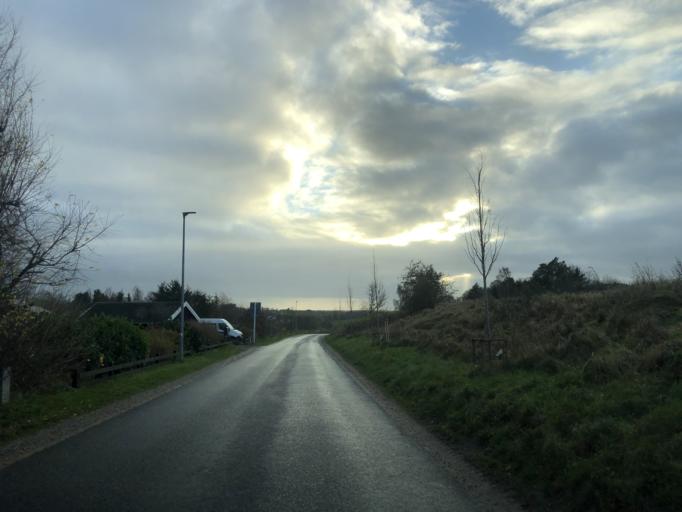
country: DK
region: Central Jutland
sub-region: Viborg Kommune
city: Viborg
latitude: 56.4783
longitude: 9.3420
